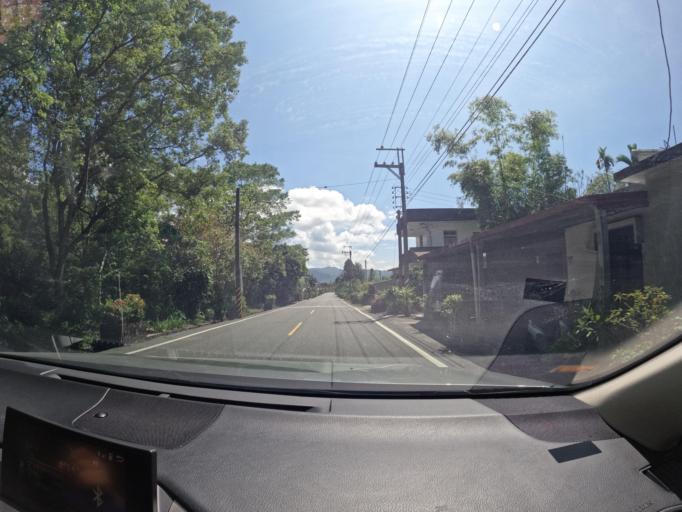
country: TW
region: Taiwan
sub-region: Hualien
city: Hualian
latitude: 23.5840
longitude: 121.3644
